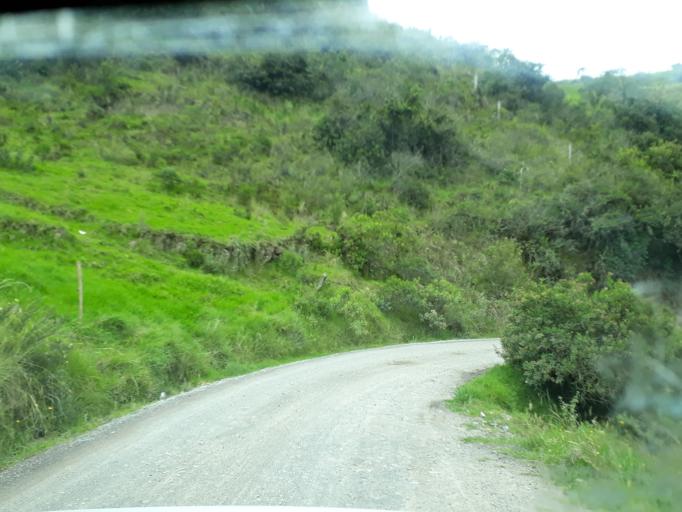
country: CO
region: Cundinamarca
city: Carmen de Carupa
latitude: 5.3170
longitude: -73.8933
